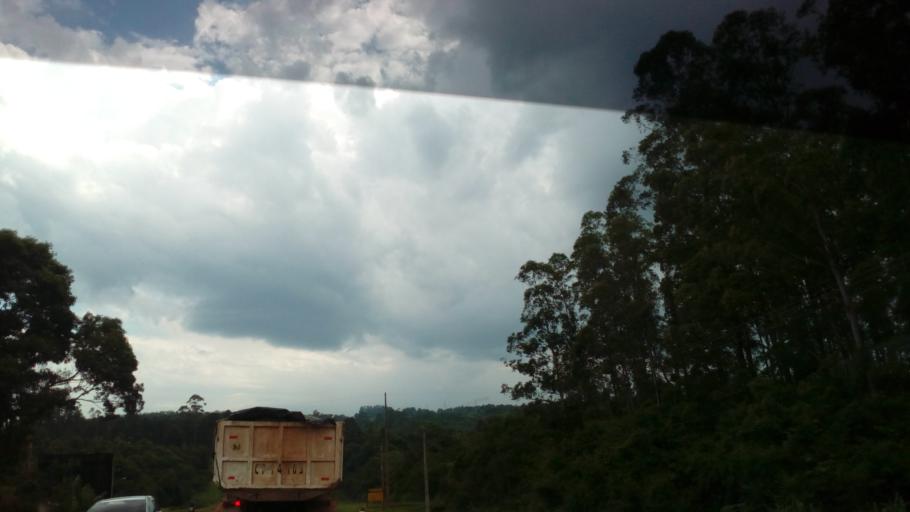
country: PY
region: Itapua
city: Obligado
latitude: -27.0636
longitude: -55.6031
